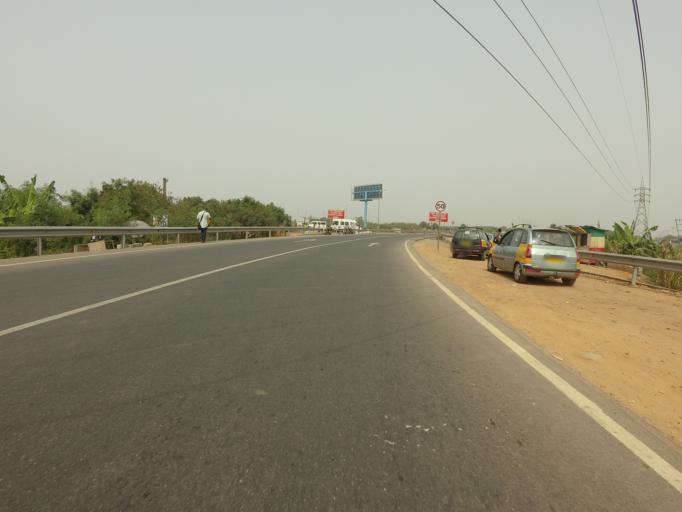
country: GH
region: Greater Accra
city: Nungua
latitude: 5.6601
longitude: -0.0759
